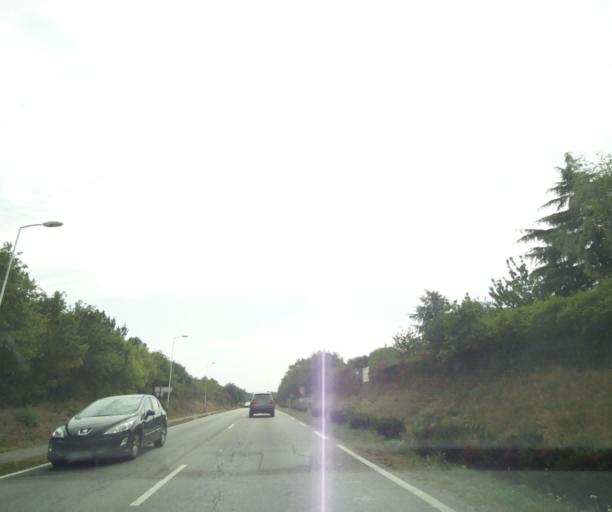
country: FR
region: Pays de la Loire
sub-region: Departement de la Loire-Atlantique
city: Saint-Herblain
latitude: 47.2138
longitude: -1.6362
